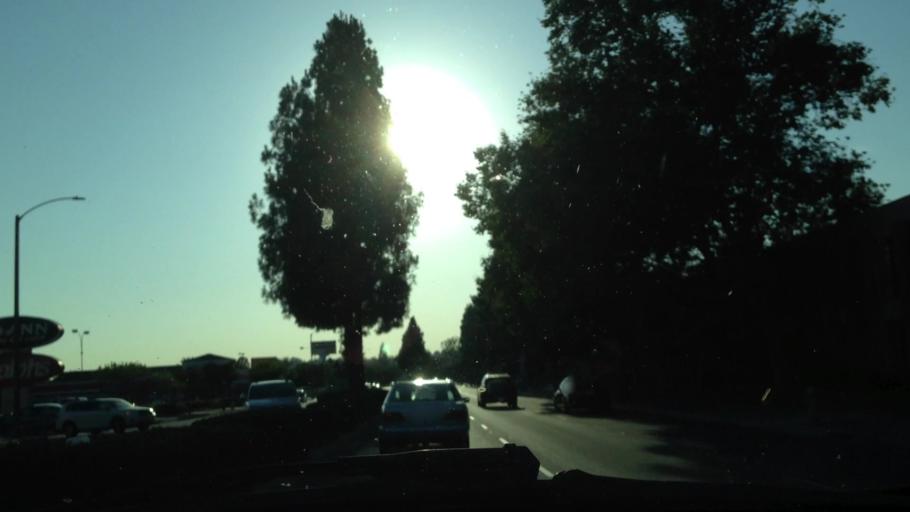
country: US
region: California
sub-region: Orange County
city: Placentia
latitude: 33.8882
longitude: -117.8661
